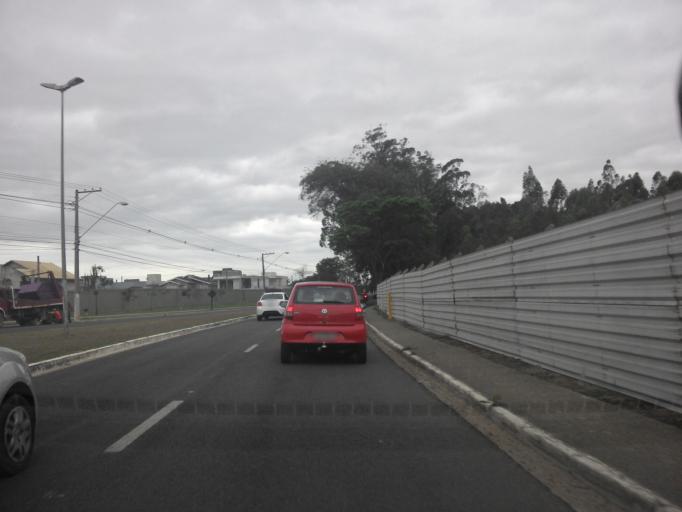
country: BR
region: Sao Paulo
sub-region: Taubate
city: Taubate
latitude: -23.0272
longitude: -45.6025
